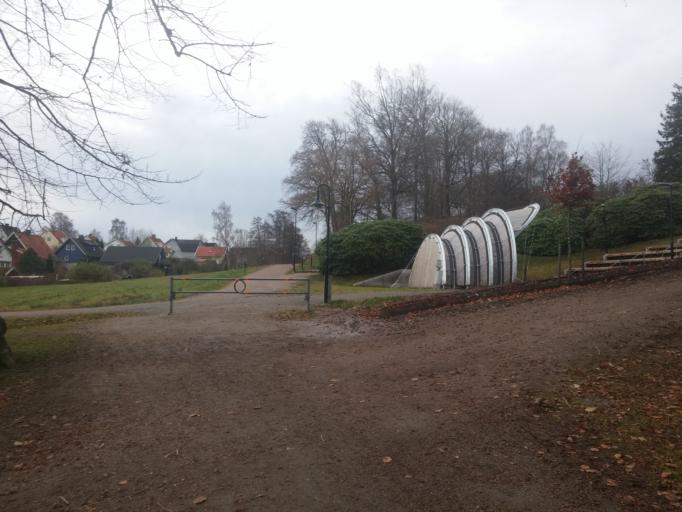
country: SE
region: Halland
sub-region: Laholms Kommun
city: Laholm
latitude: 56.5085
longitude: 13.0451
